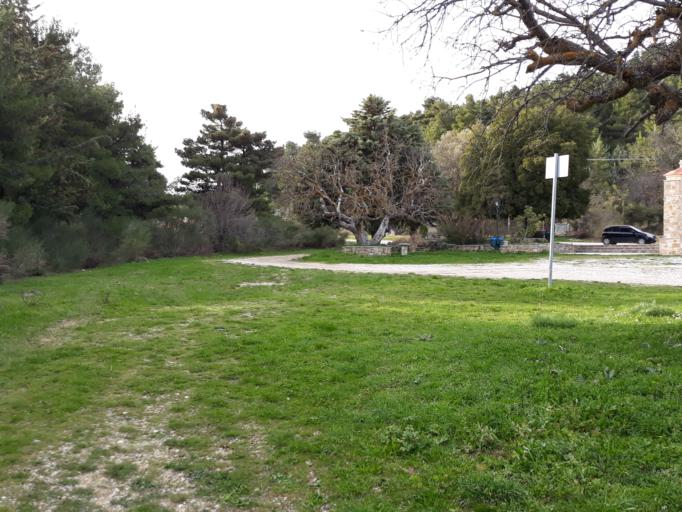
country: GR
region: Attica
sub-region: Nomarchia Anatolikis Attikis
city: Afidnes
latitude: 38.2104
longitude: 23.8100
